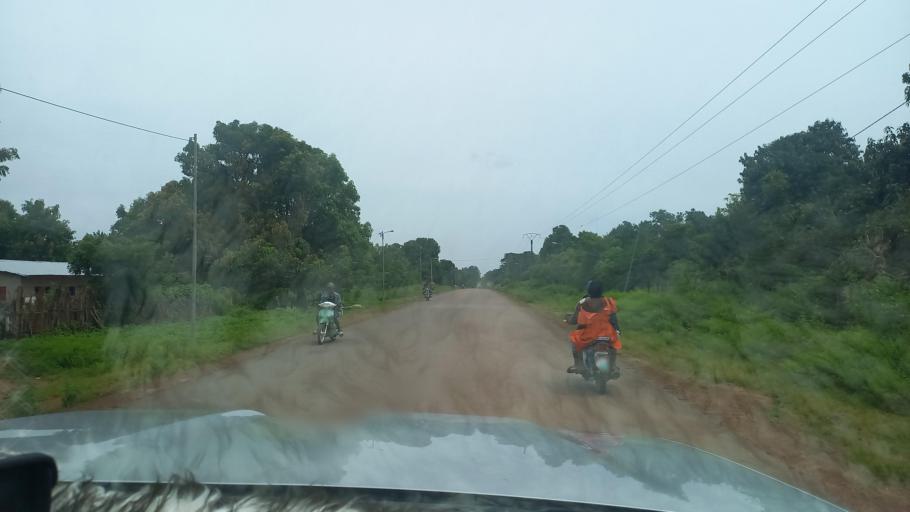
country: SN
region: Ziguinchor
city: Bignona
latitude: 12.8189
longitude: -16.1816
